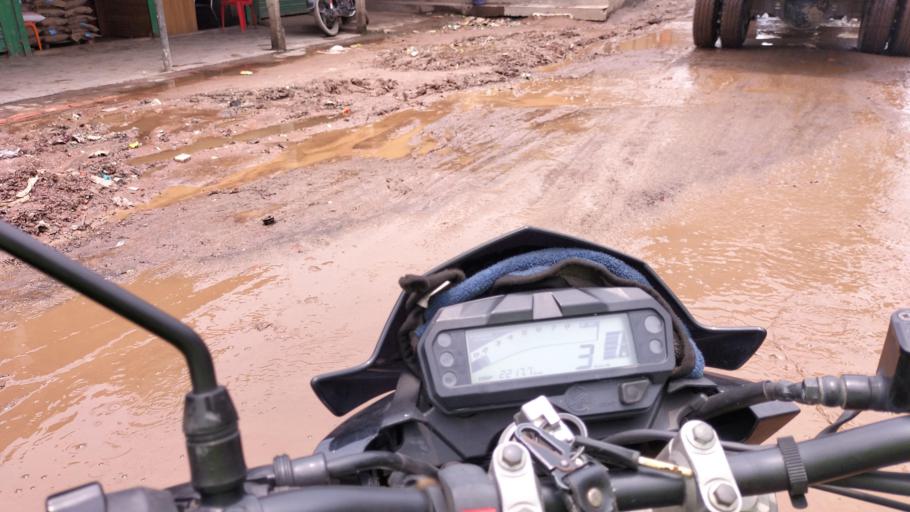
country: BD
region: Dhaka
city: Mymensingh
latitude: 24.7636
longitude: 90.4513
